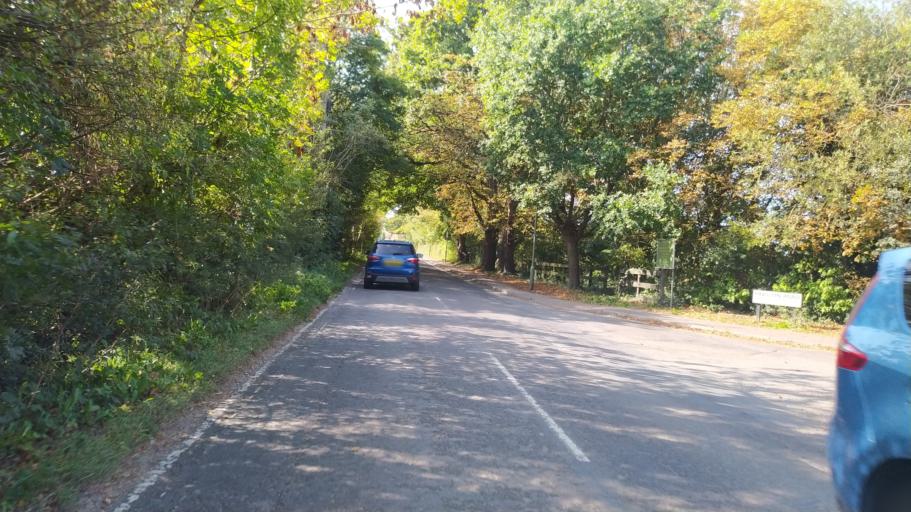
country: GB
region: England
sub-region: Hampshire
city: Hedge End
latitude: 50.9185
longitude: -1.2891
